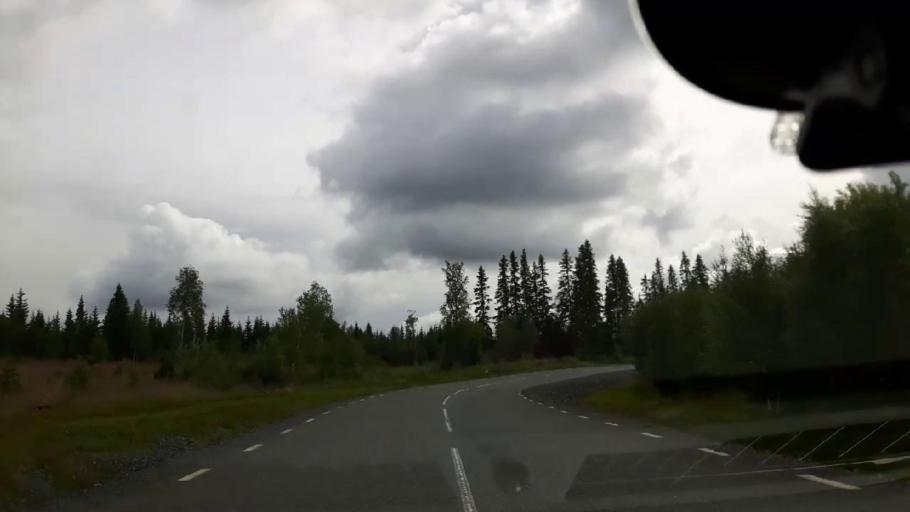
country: SE
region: Jaemtland
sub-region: Krokoms Kommun
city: Valla
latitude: 63.4819
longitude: 13.8580
